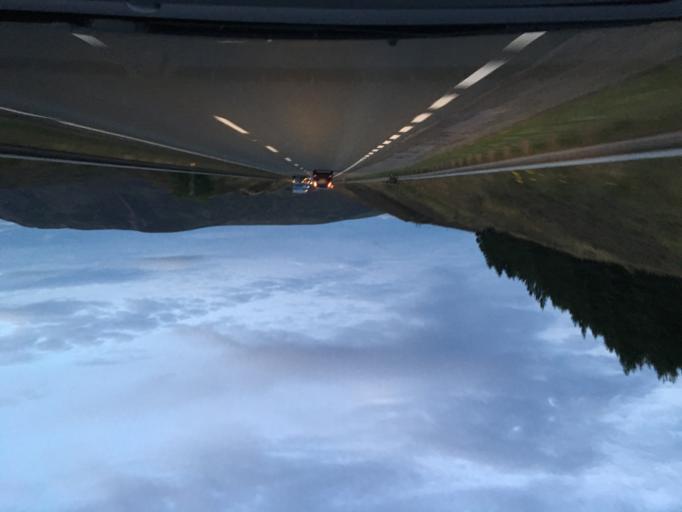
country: GB
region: Scotland
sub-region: Highland
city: Kingussie
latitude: 56.8439
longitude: -4.2383
